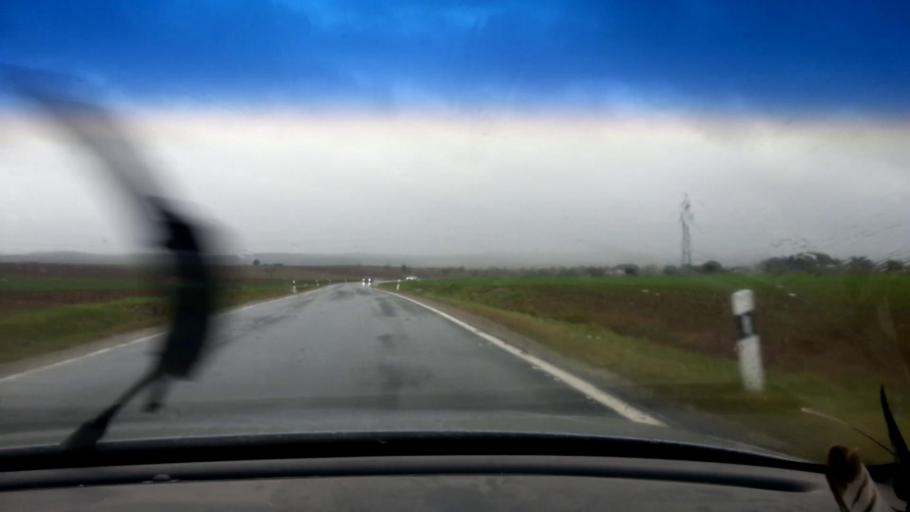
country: DE
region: Bavaria
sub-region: Upper Franconia
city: Burgebrach
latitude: 49.8649
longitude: 10.7371
